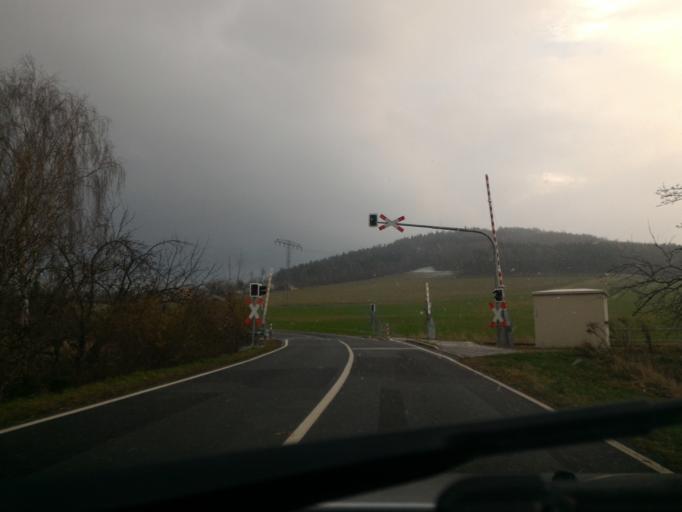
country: DE
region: Saxony
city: Grossschonau
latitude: 50.8937
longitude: 14.6908
